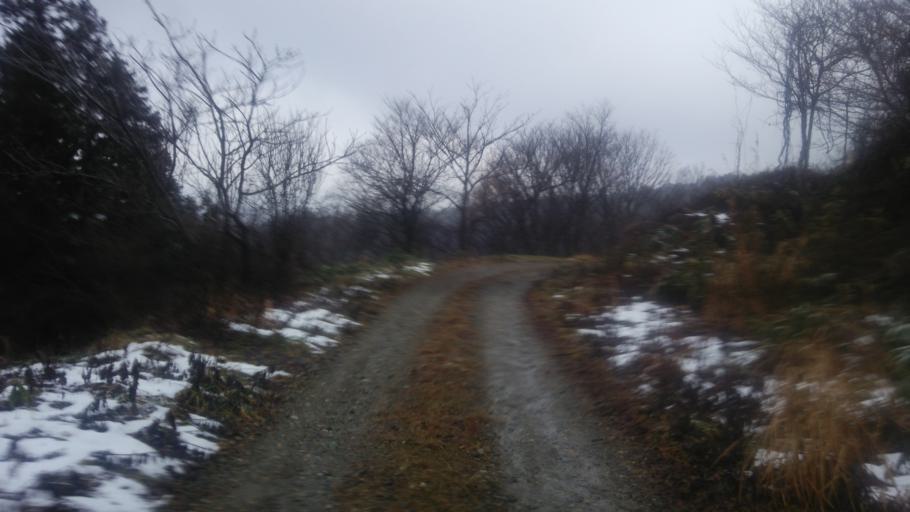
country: JP
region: Fukushima
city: Inawashiro
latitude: 37.5757
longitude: 139.9862
